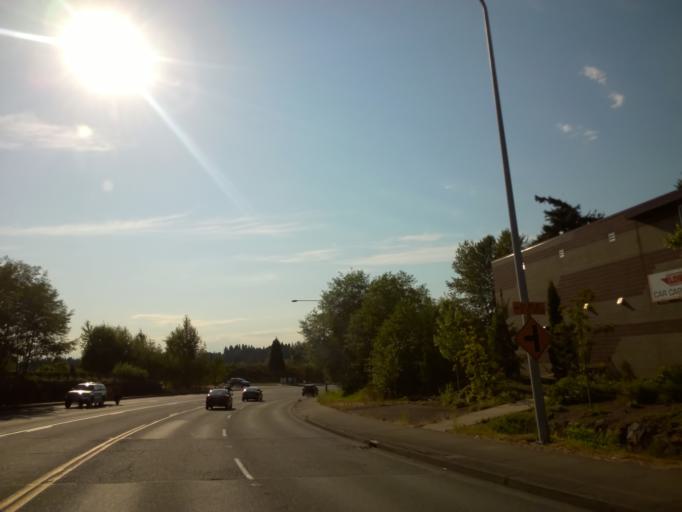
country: US
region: Washington
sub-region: King County
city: Woodinville
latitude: 47.7658
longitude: -122.1498
